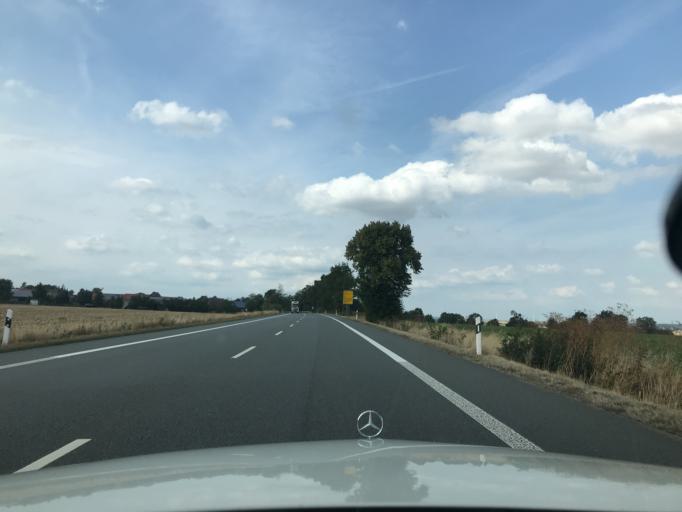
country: DE
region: North Rhine-Westphalia
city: Warburg
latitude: 51.5298
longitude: 9.1419
